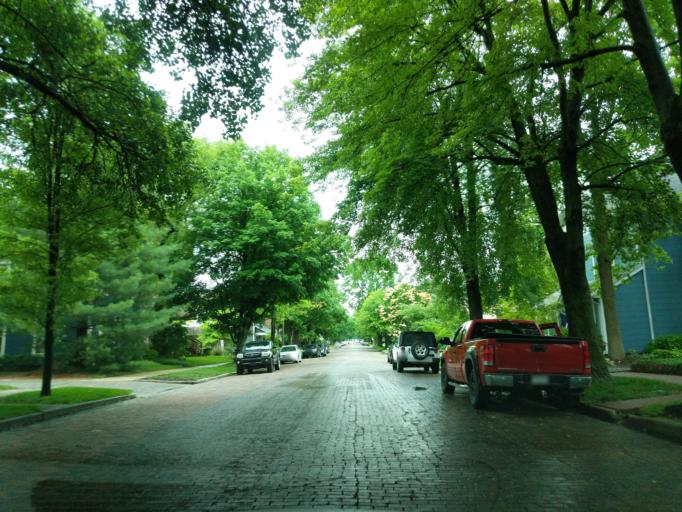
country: US
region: Indiana
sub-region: Hamilton County
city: Noblesville
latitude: 40.0465
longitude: -86.0095
